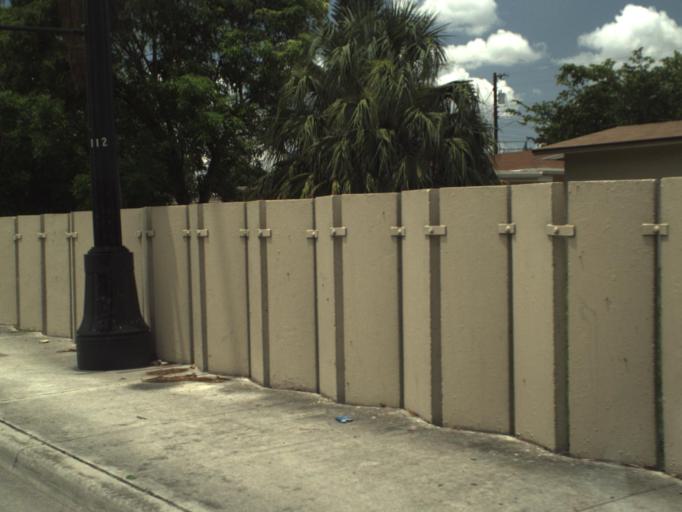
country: US
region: Florida
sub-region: Broward County
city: Lauderhill
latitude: 26.1210
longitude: -80.2161
